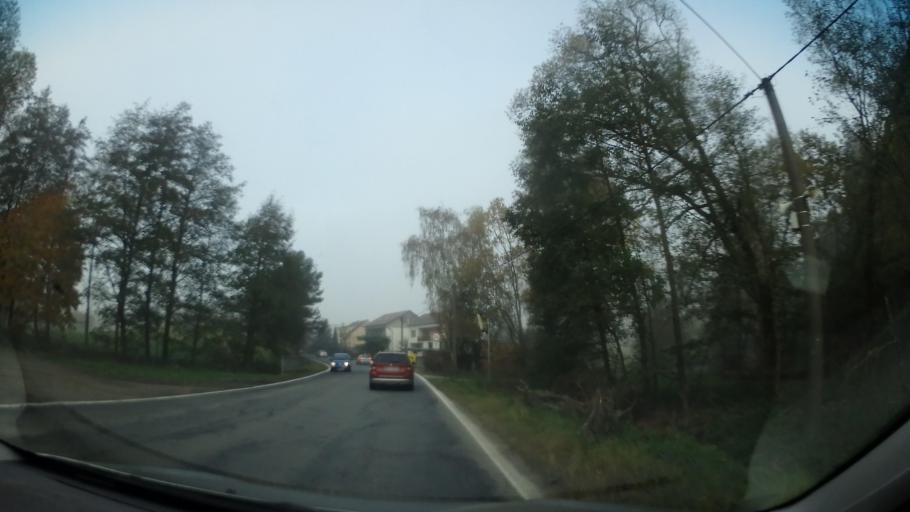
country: CZ
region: Vysocina
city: Krizanov
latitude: 49.4710
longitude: 16.1260
